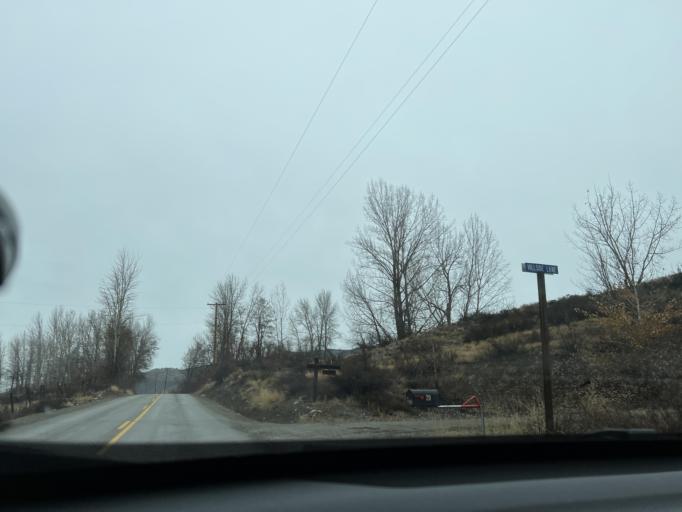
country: US
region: Washington
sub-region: Okanogan County
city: Brewster
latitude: 48.4997
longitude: -120.1748
